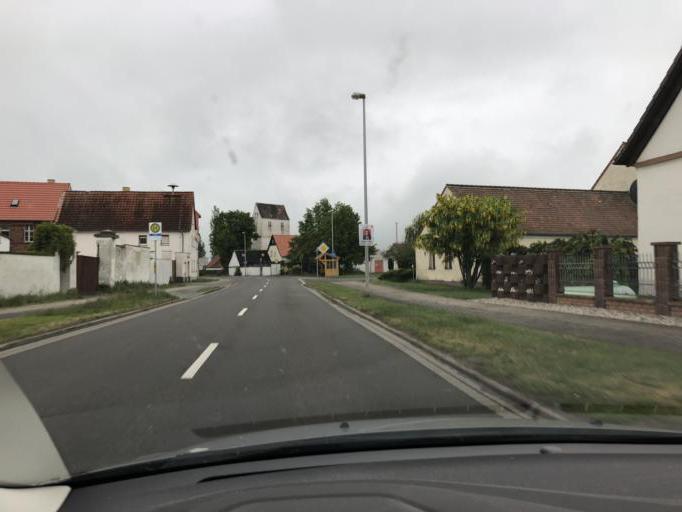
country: DE
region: Saxony
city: Krostitz
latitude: 51.4844
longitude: 12.4131
